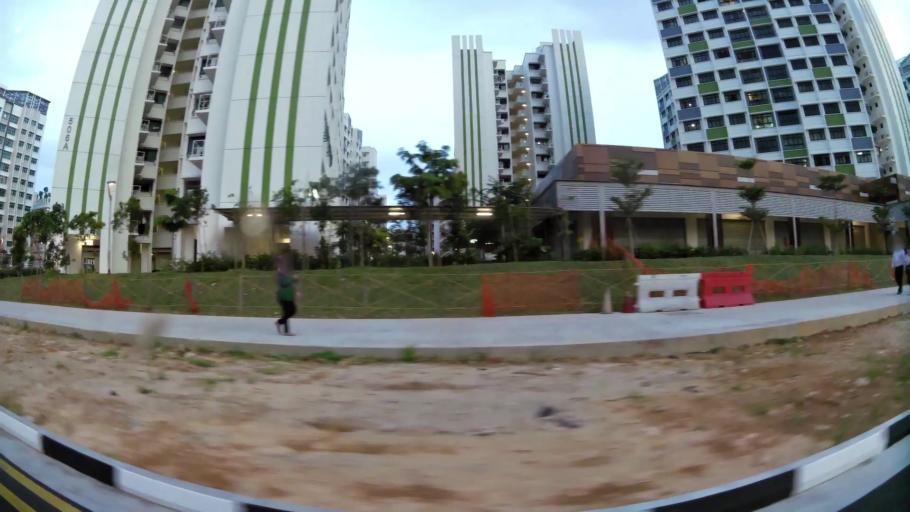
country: MY
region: Johor
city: Kampung Pasir Gudang Baru
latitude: 1.4160
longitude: 103.8395
